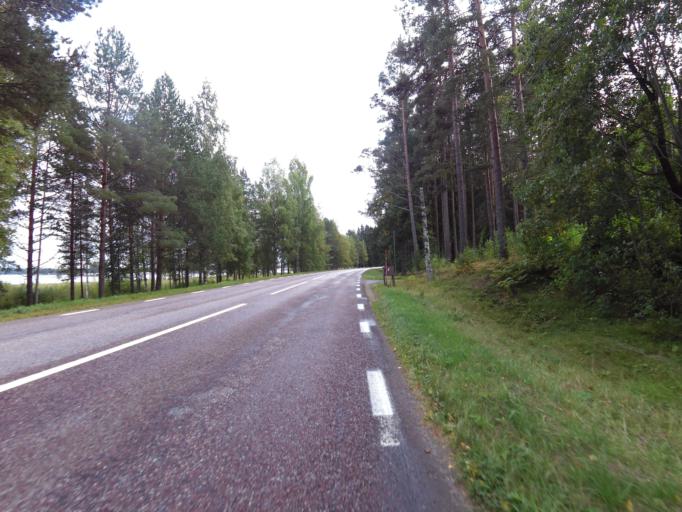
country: SE
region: Gaevleborg
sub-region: Sandvikens Kommun
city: Sandviken
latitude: 60.7075
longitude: 16.8110
